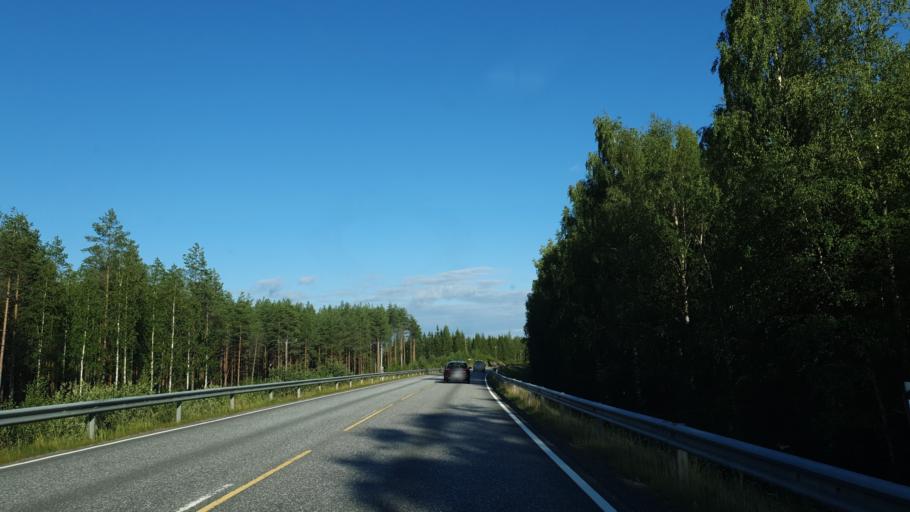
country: FI
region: North Karelia
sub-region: Joensuu
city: Outokumpu
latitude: 62.5321
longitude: 28.9765
